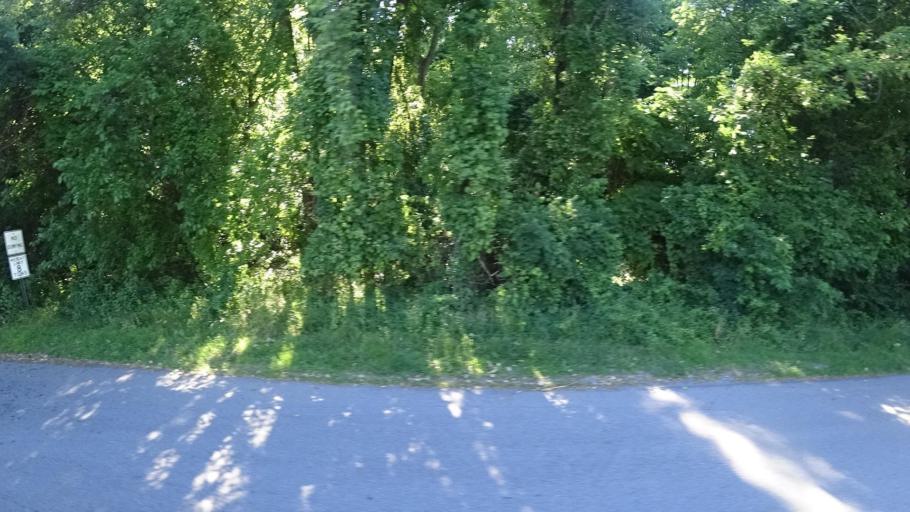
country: US
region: Indiana
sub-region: Porter County
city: Burns Harbor
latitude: 41.6177
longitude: -87.1435
